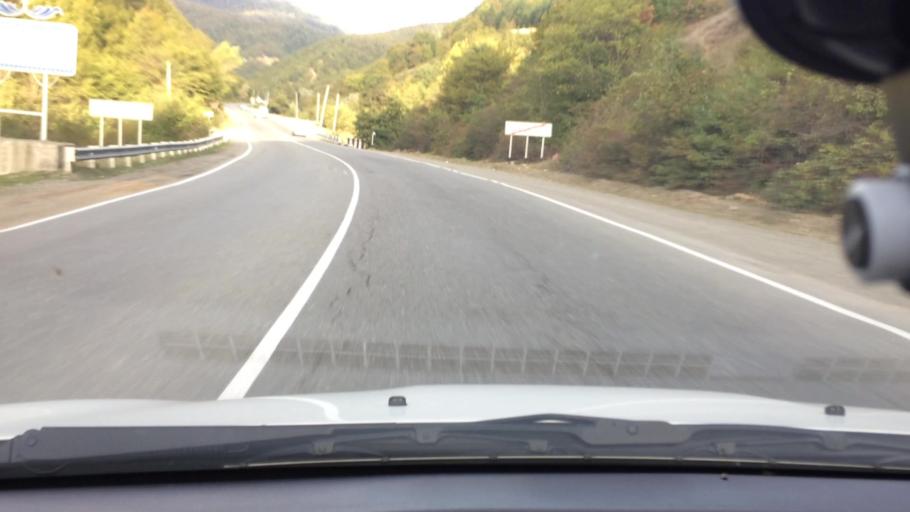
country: GE
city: Surami
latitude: 42.0377
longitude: 43.5177
